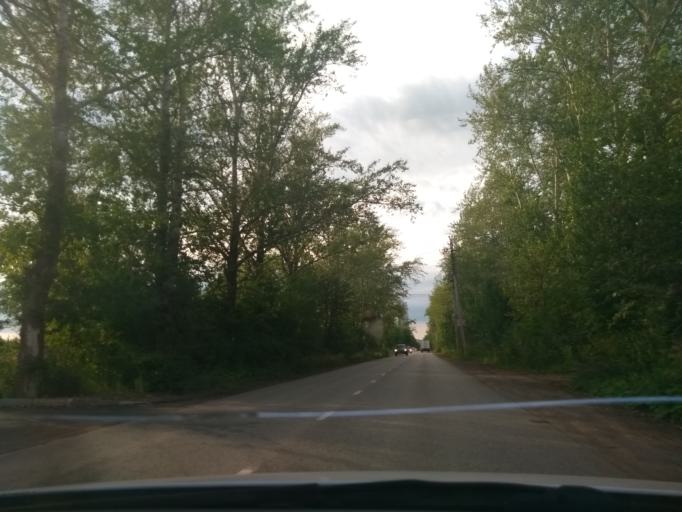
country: RU
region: Perm
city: Perm
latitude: 57.9990
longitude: 56.3341
